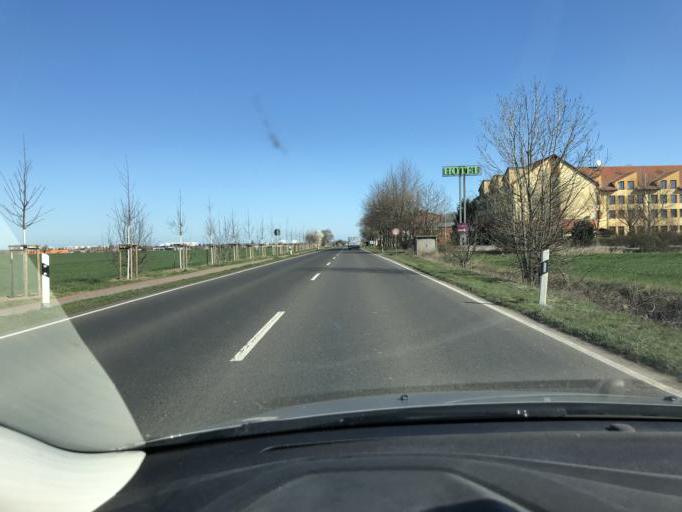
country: DE
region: Saxony-Anhalt
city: Magdeburg
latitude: 52.0666
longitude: 11.6148
